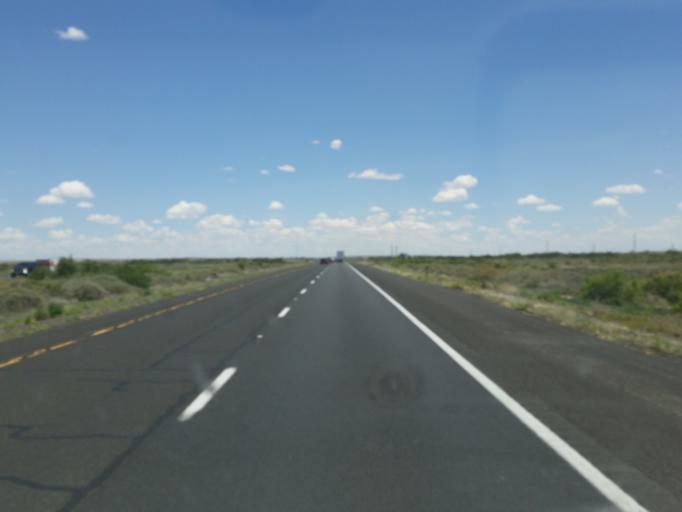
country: US
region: Arizona
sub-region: Navajo County
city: Joseph City
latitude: 34.9645
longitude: -110.4045
